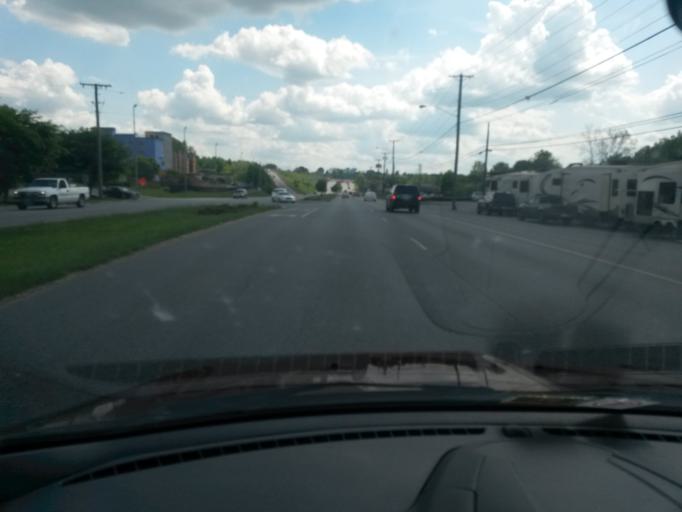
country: US
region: Virginia
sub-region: City of Lynchburg
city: West Lynchburg
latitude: 37.3482
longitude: -79.1865
